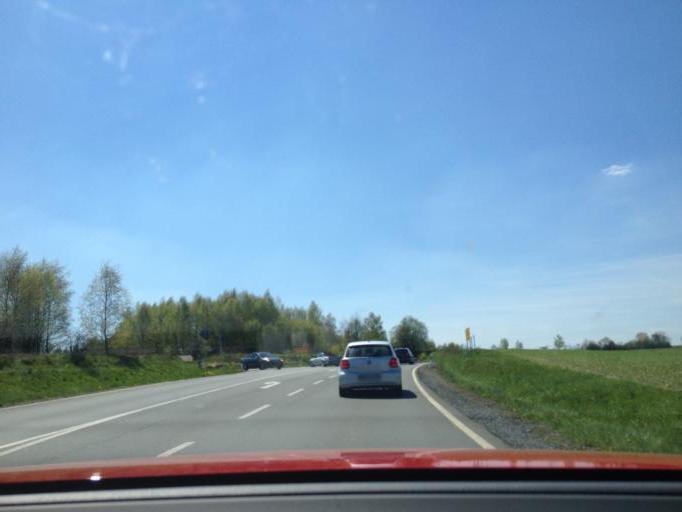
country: DE
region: Bavaria
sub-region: Upper Franconia
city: Schwarzenbach an der Saale
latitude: 50.2310
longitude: 11.9330
